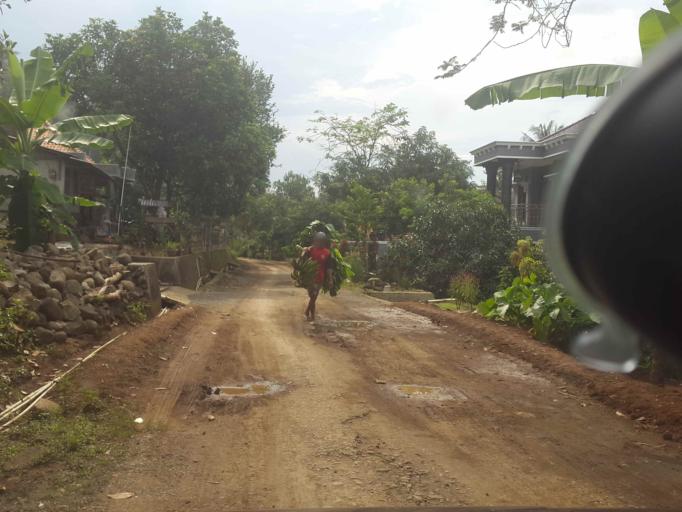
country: ID
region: Central Java
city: Kaliduren
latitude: -7.5564
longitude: 109.0924
